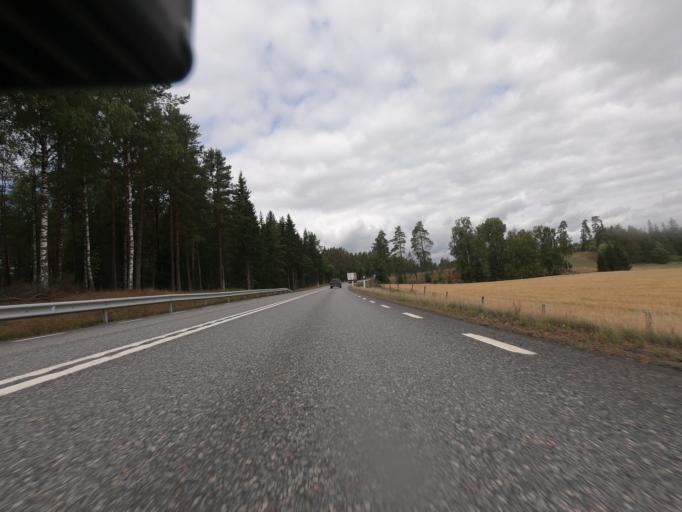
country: SE
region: Joenkoeping
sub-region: Vaggeryds Kommun
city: Vaggeryd
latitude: 57.4867
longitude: 14.3003
